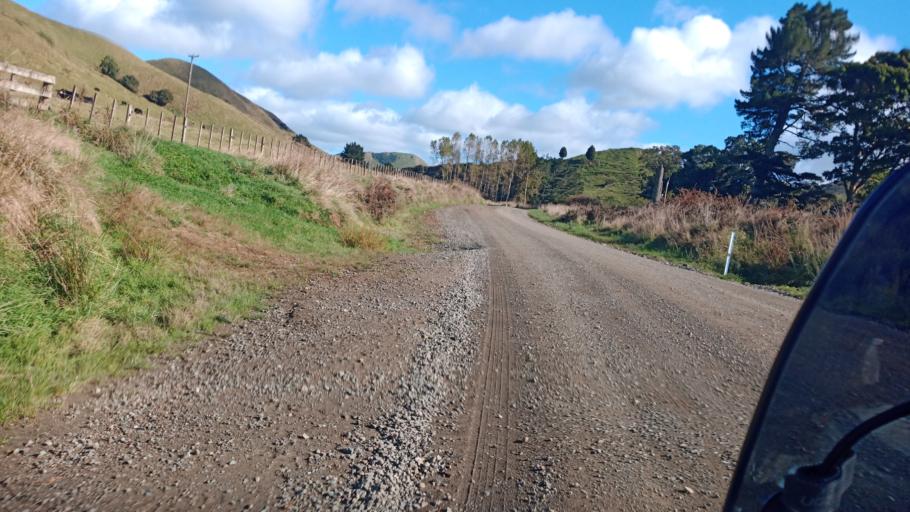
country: NZ
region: Bay of Plenty
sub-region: Opotiki District
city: Opotiki
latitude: -38.4636
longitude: 177.4265
